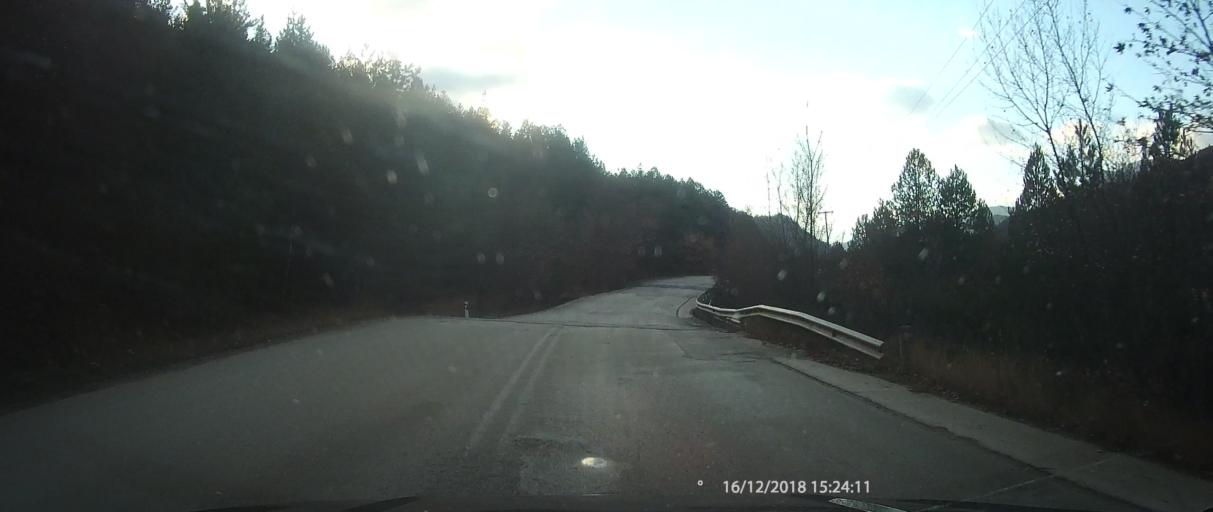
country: GR
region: Epirus
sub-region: Nomos Ioanninon
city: Konitsa
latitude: 40.1401
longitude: 20.7952
